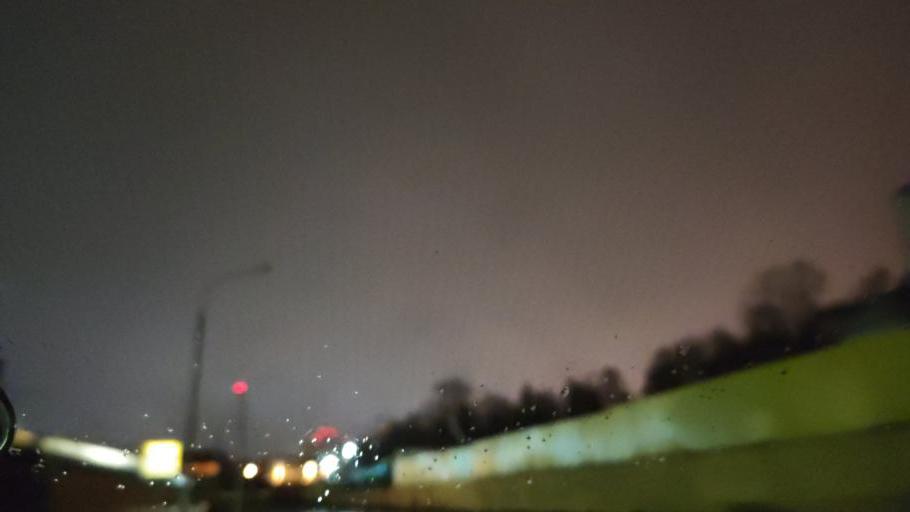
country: RU
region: Moskovskaya
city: Marfino
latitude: 55.6982
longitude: 37.3887
